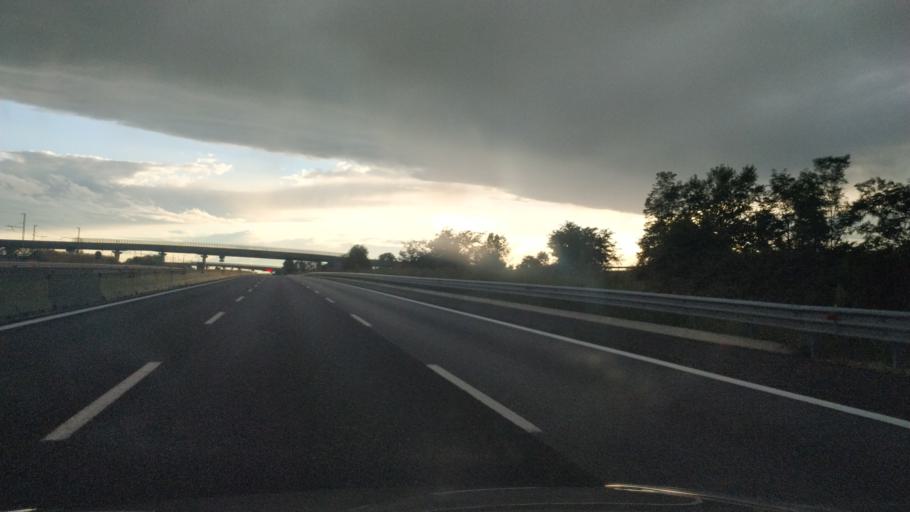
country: IT
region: Piedmont
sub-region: Provincia di Vercelli
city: Greggio
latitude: 45.4599
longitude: 8.3639
